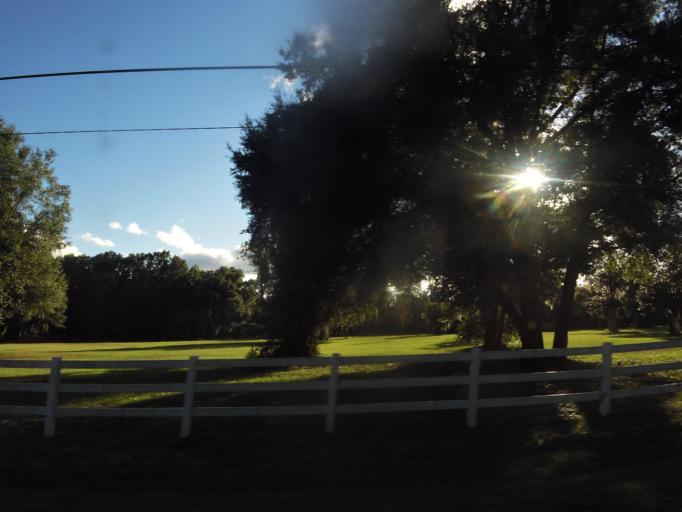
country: US
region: Florida
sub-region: Marion County
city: Citra
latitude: 29.4634
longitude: -82.1443
